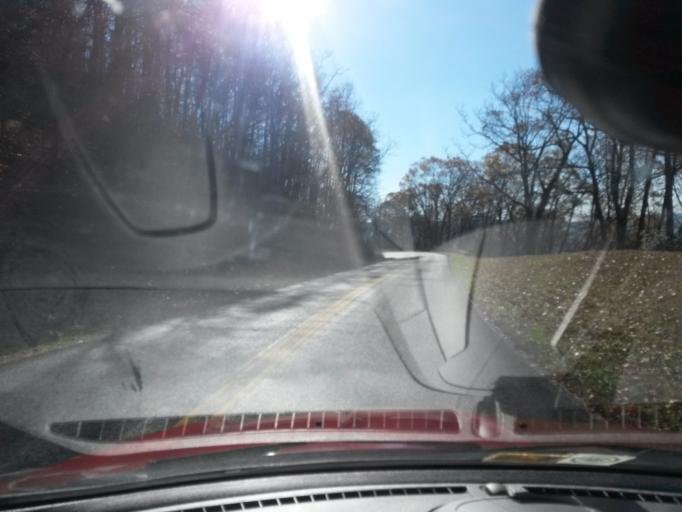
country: US
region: Virginia
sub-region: Botetourt County
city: Buchanan
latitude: 37.4791
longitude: -79.6533
